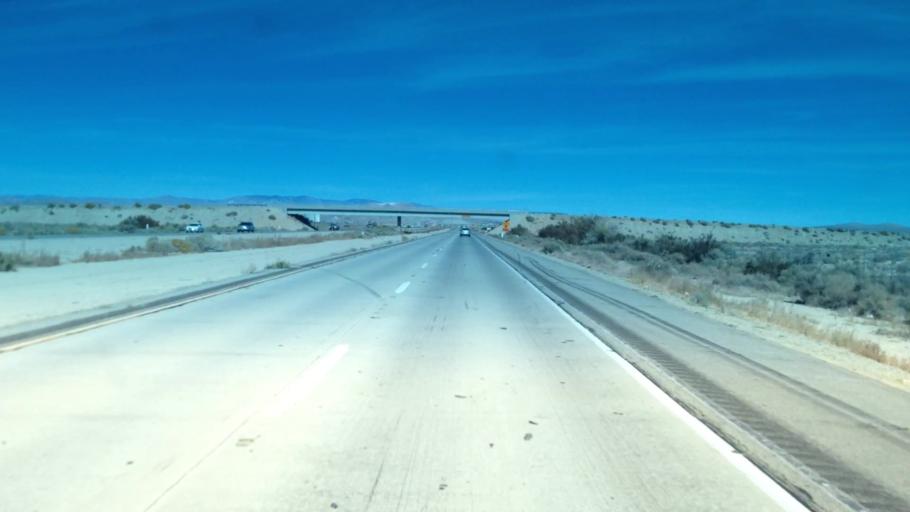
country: US
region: California
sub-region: Kern County
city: Rosamond
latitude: 34.7888
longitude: -118.1705
